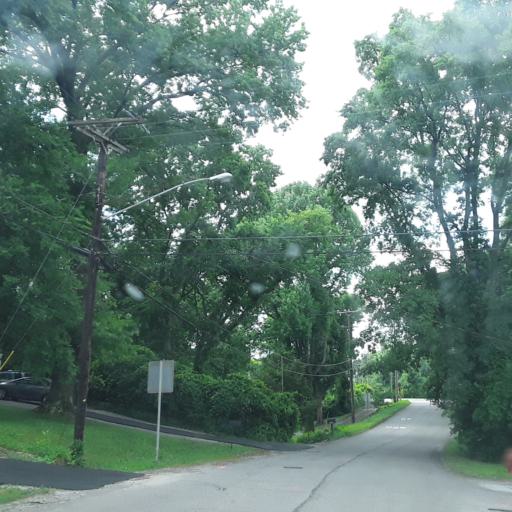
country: US
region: Tennessee
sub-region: Davidson County
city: Oak Hill
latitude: 36.1111
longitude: -86.7332
